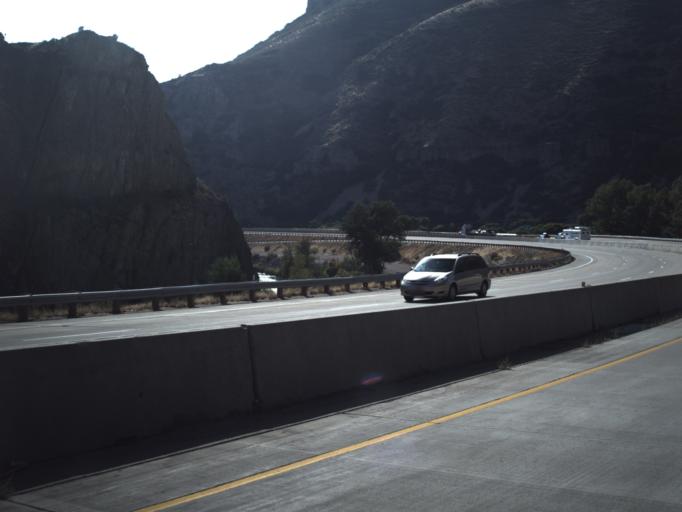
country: US
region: Utah
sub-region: Morgan County
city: Morgan
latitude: 41.0598
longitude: -111.5877
